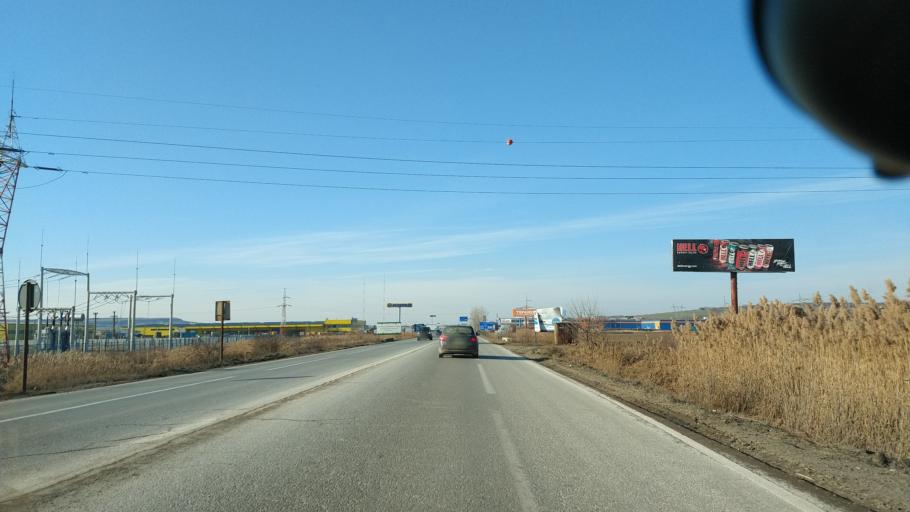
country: RO
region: Iasi
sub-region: Comuna Valea Lupului
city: Valea Lupului
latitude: 47.1790
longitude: 27.4816
